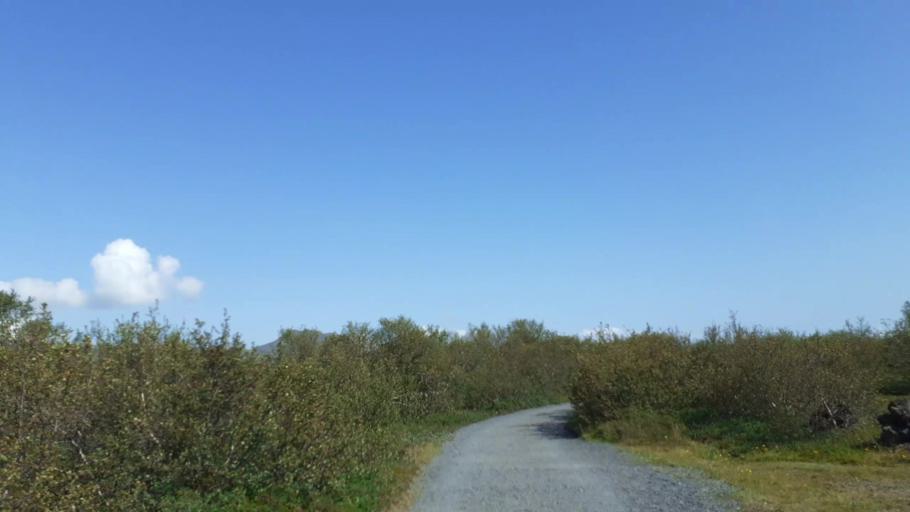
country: IS
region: West
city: Borgarnes
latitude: 64.7530
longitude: -21.5513
